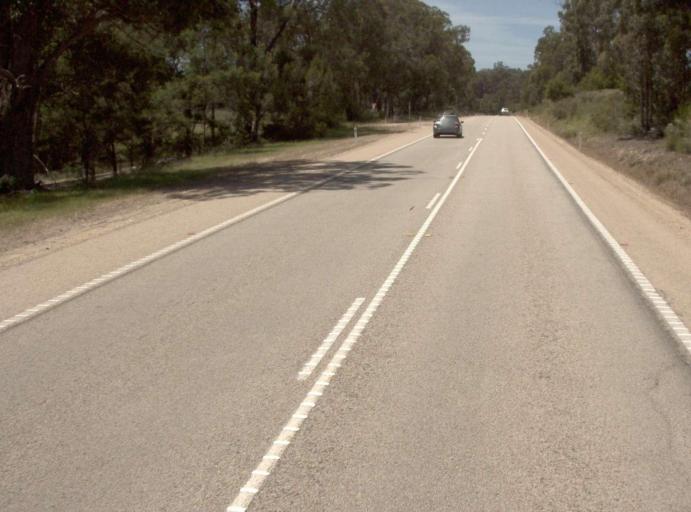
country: AU
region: Victoria
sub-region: East Gippsland
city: Bairnsdale
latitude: -37.7518
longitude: 147.7434
